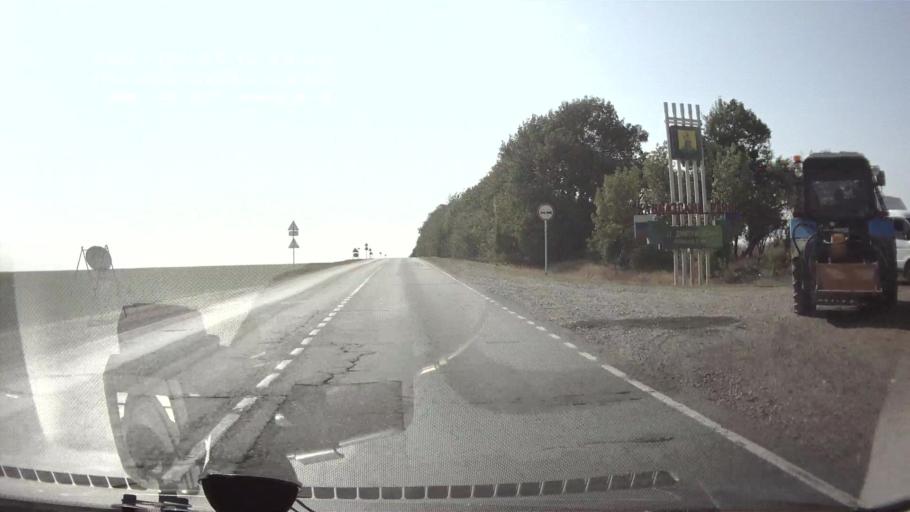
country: RU
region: Krasnodarskiy
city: Dmitriyevskaya
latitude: 45.6734
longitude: 40.7440
